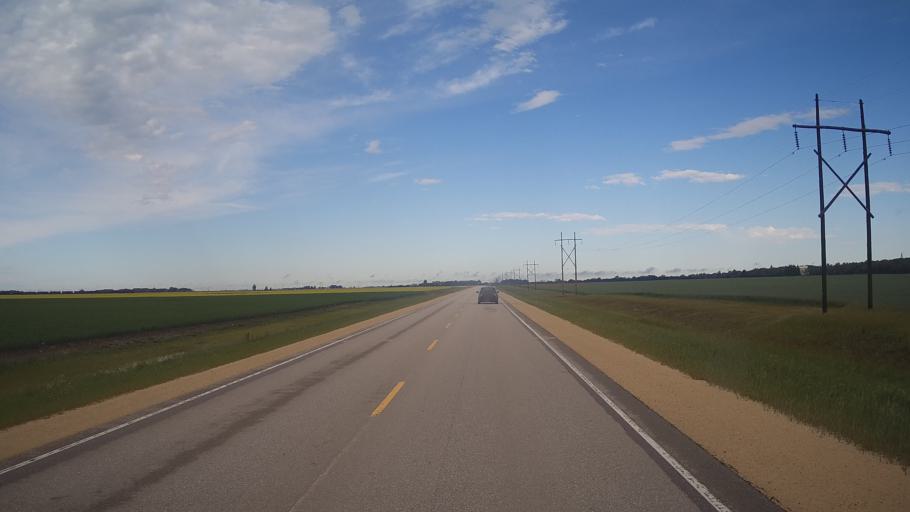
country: CA
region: Manitoba
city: Stonewall
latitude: 50.1231
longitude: -97.5105
